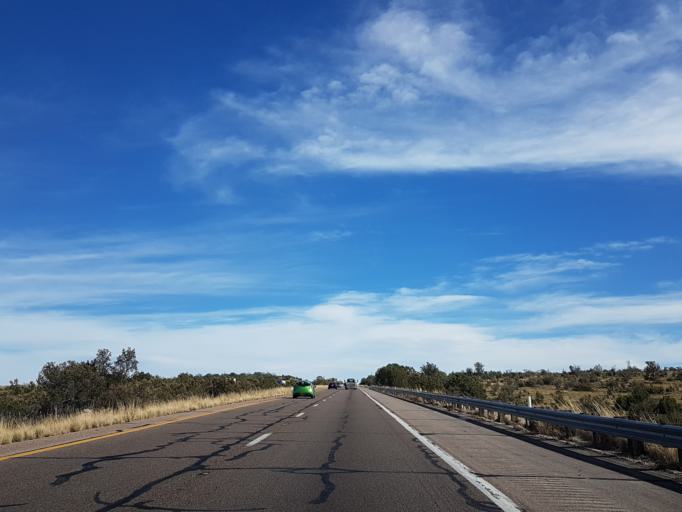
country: US
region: Arizona
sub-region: Yavapai County
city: Paulden
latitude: 35.2817
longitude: -112.7904
